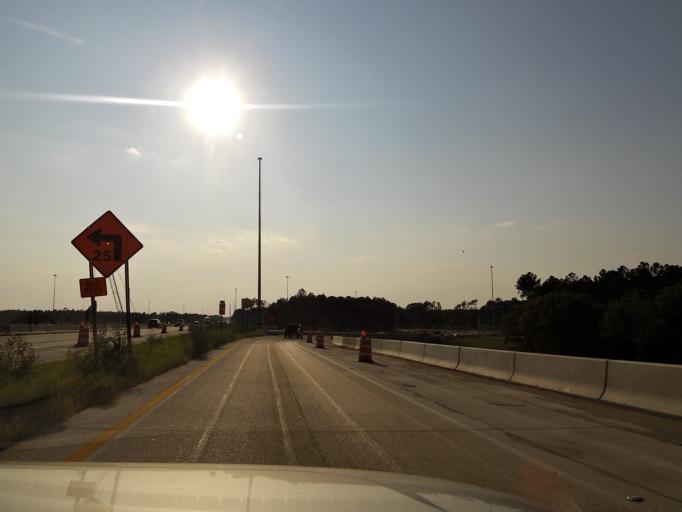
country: US
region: Florida
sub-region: Duval County
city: Baldwin
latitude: 30.2895
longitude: -81.9802
